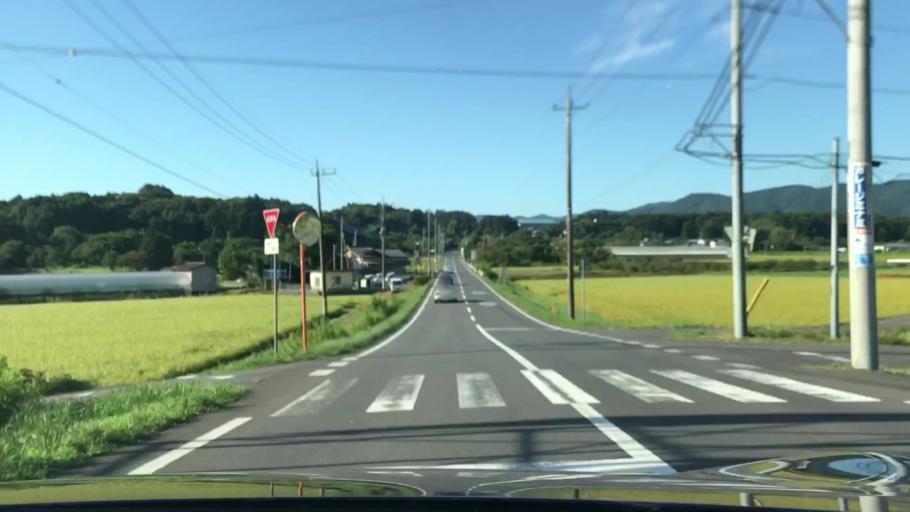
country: JP
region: Ibaraki
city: Makabe
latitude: 36.2388
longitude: 140.1647
